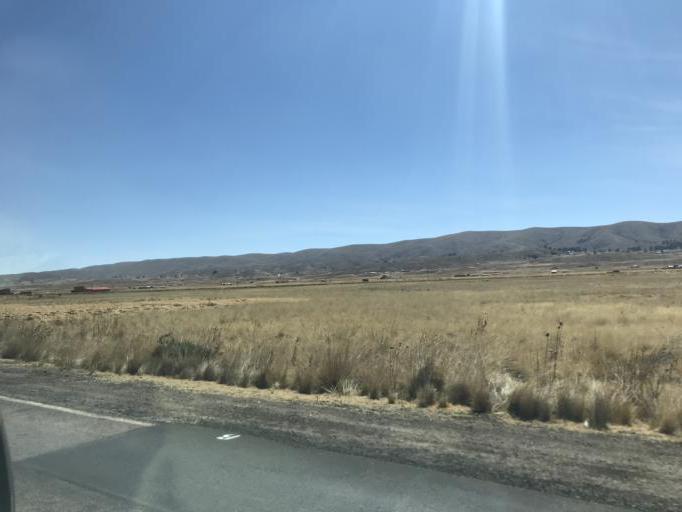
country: BO
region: La Paz
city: Tiahuanaco
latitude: -16.5914
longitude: -68.5819
